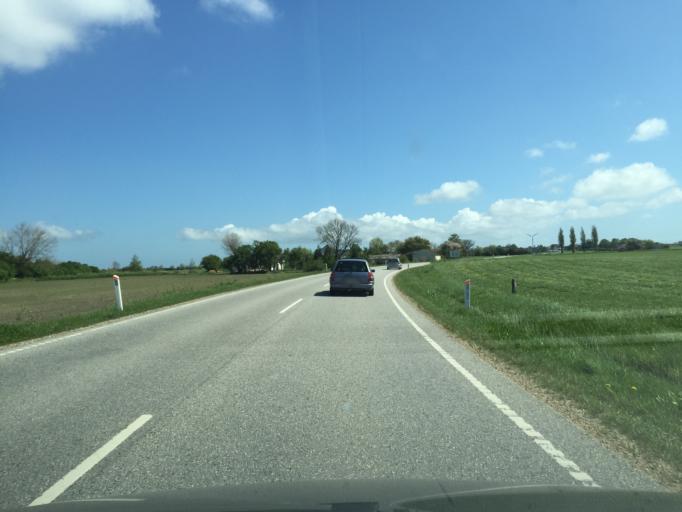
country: DK
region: Zealand
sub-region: Vordingborg Kommune
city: Stege
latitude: 54.9680
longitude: 12.2141
